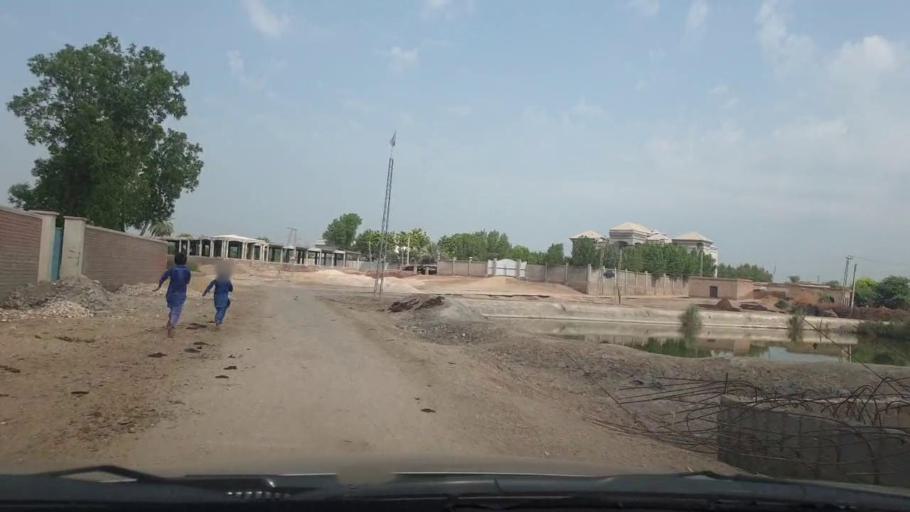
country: PK
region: Sindh
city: Larkana
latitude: 27.6641
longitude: 68.1820
